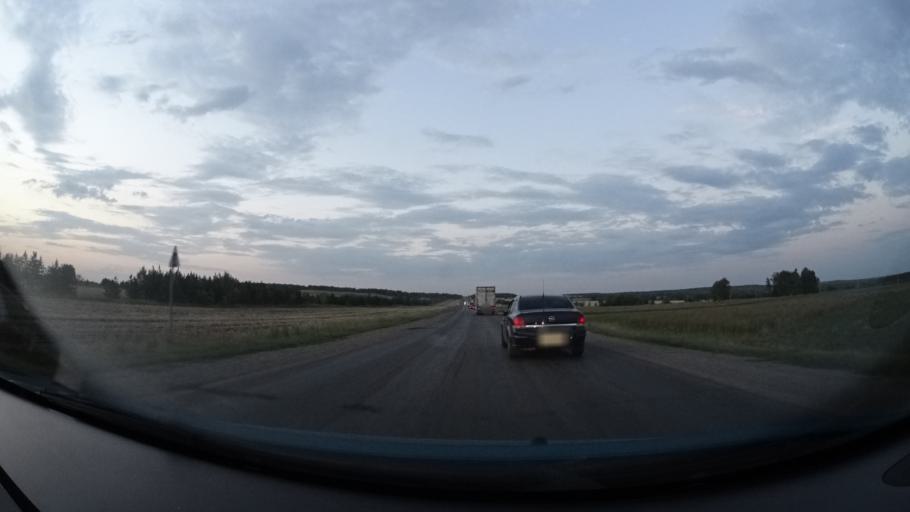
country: RU
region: Tatarstan
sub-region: Bavlinskiy Rayon
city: Bavly
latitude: 54.2738
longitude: 52.9821
